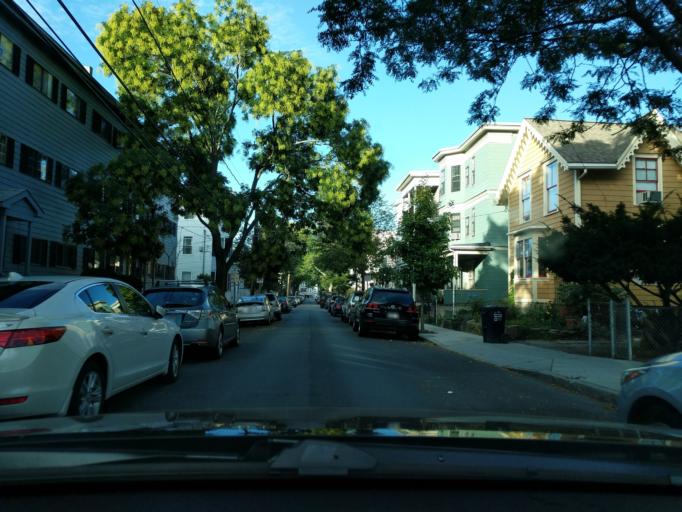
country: US
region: Massachusetts
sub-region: Middlesex County
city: Cambridge
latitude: 42.3713
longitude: -71.1009
